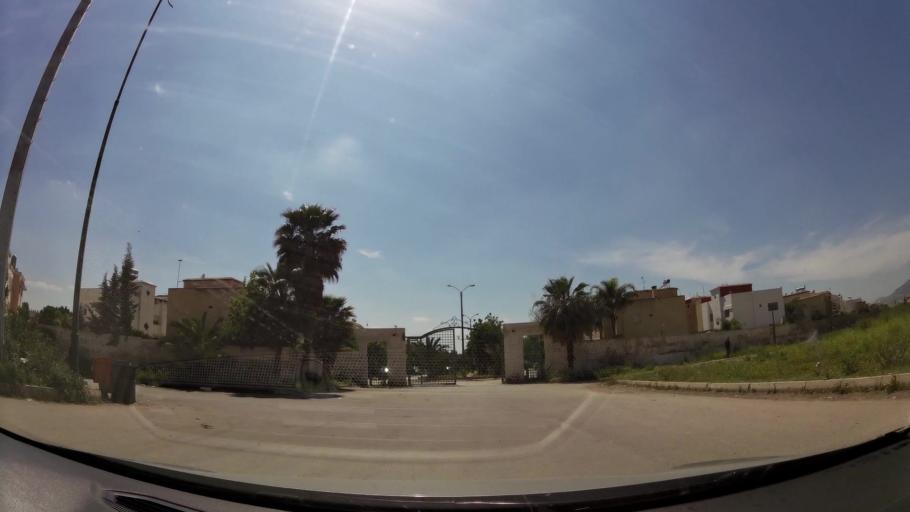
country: MA
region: Fes-Boulemane
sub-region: Fes
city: Fes
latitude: 34.0160
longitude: -5.0224
